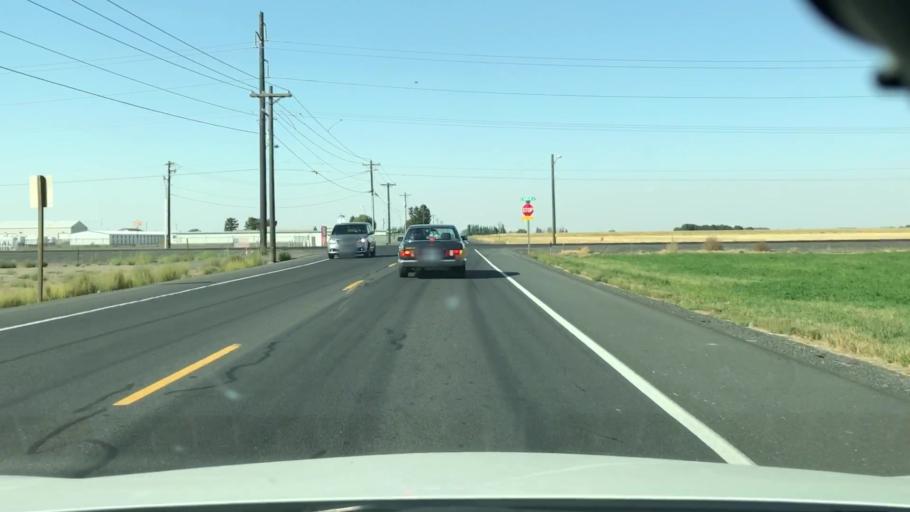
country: US
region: Washington
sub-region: Grant County
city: Moses Lake
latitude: 47.1303
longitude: -119.2358
